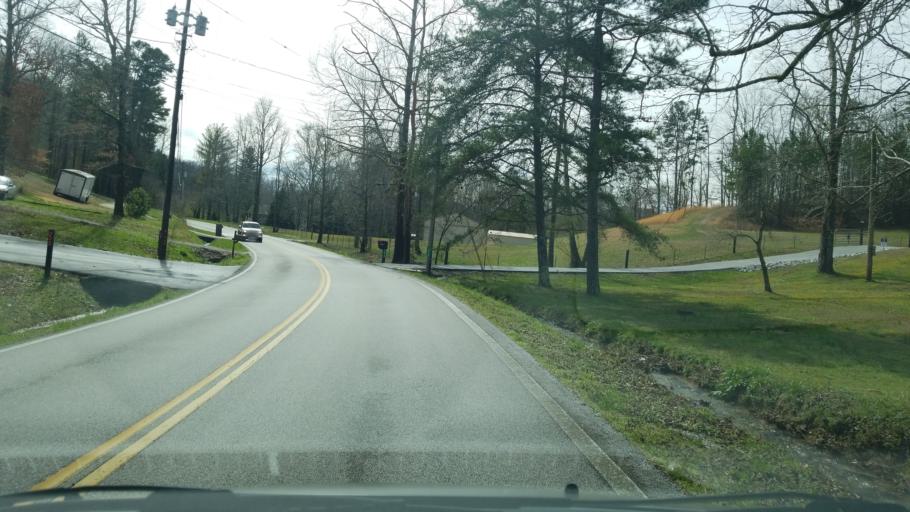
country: US
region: Tennessee
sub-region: Hamilton County
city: Harrison
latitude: 35.1344
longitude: -85.0842
